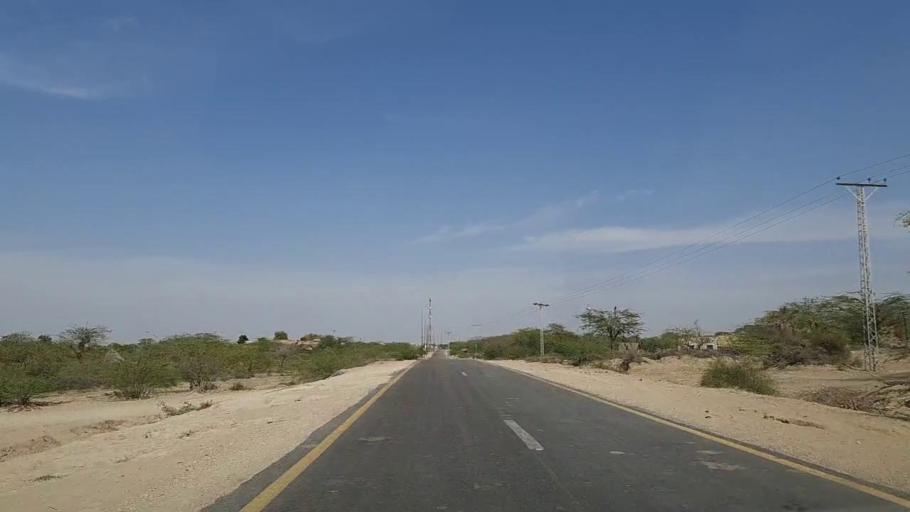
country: PK
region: Sindh
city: Mithi
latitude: 24.9706
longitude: 69.9144
